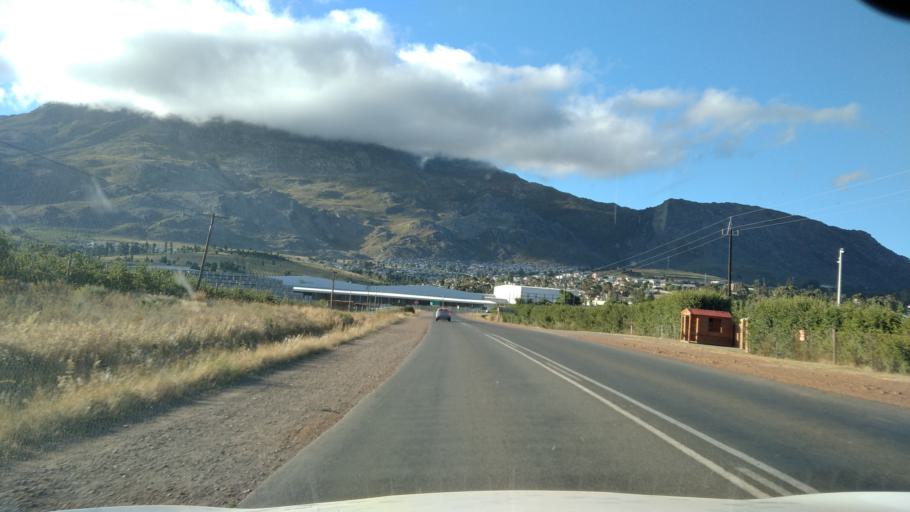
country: ZA
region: Western Cape
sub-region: Overberg District Municipality
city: Caledon
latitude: -33.9987
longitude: 19.2871
